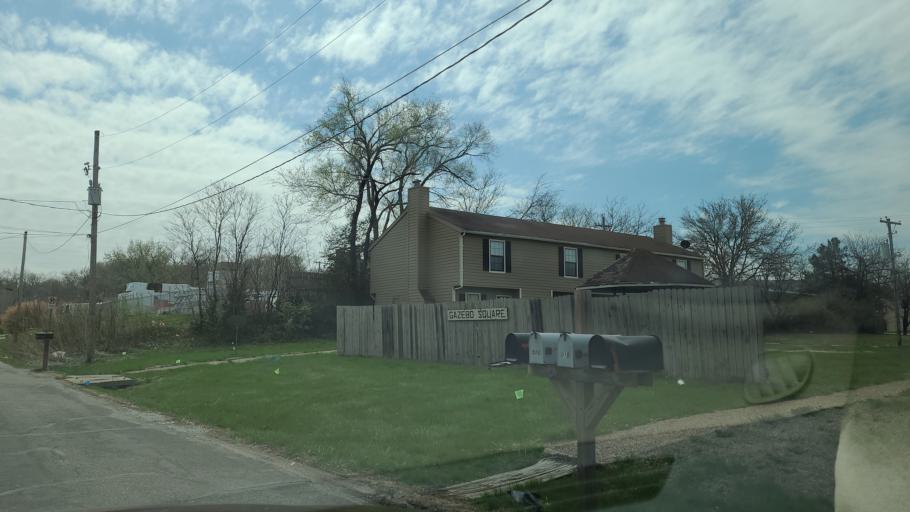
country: US
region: Kansas
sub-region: Douglas County
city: Lawrence
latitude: 38.9747
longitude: -95.2523
